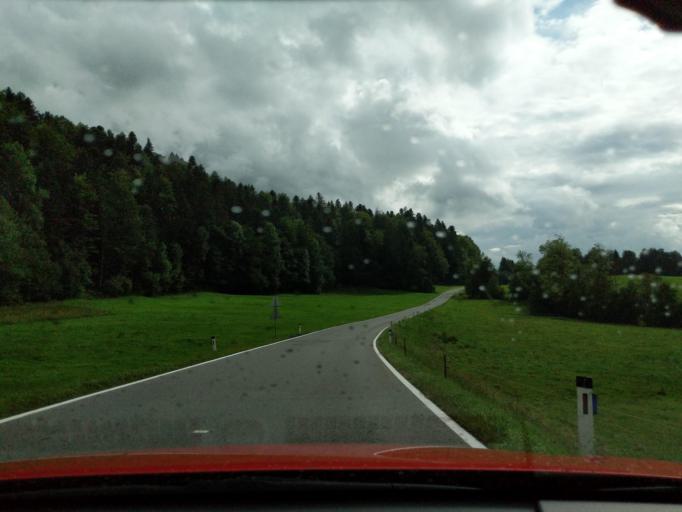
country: AT
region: Vorarlberg
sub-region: Politischer Bezirk Bregenz
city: Riefensberg
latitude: 47.5096
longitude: 9.9515
